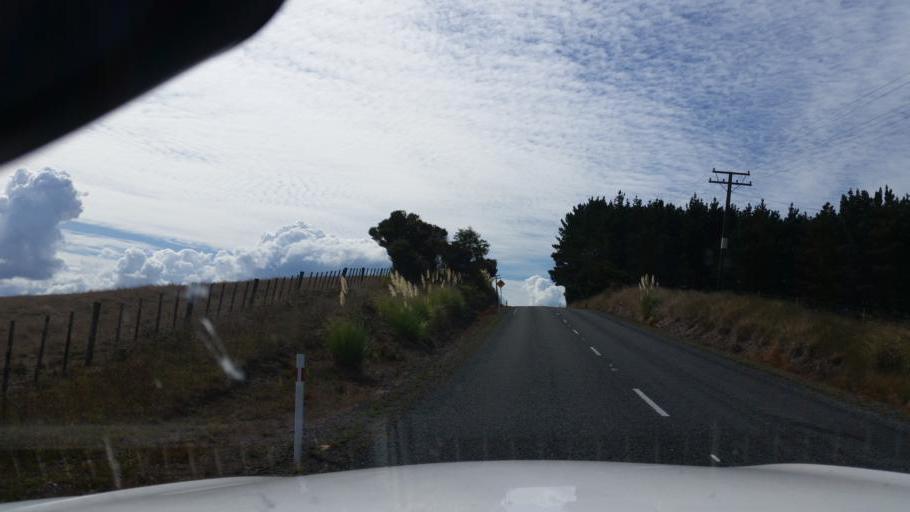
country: NZ
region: Northland
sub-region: Kaipara District
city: Dargaville
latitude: -36.1330
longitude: 174.1709
